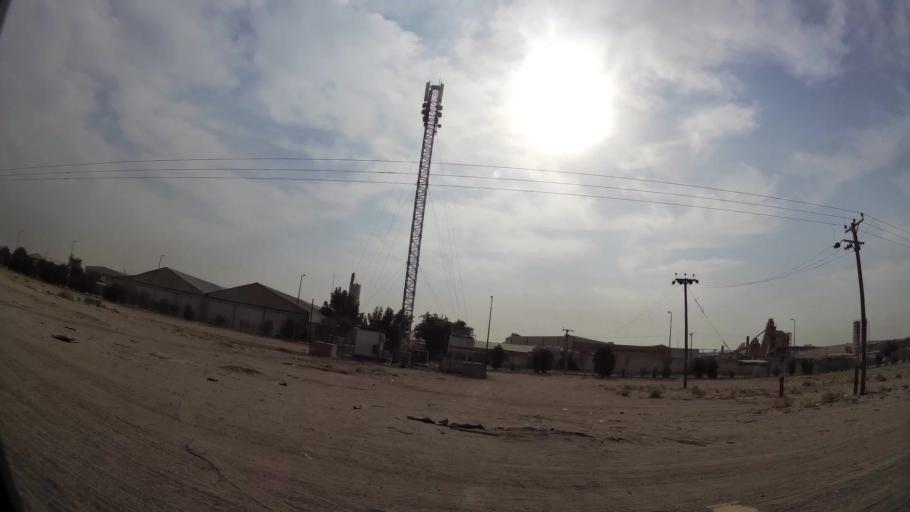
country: KW
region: Muhafazat al Jahra'
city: Al Jahra'
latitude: 29.3122
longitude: 47.7444
